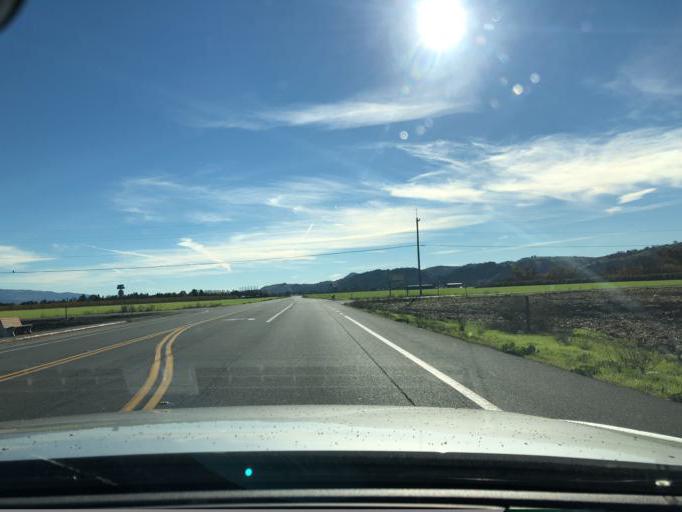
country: US
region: California
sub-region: Santa Clara County
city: Morgan Hill
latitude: 37.1918
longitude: -121.7326
